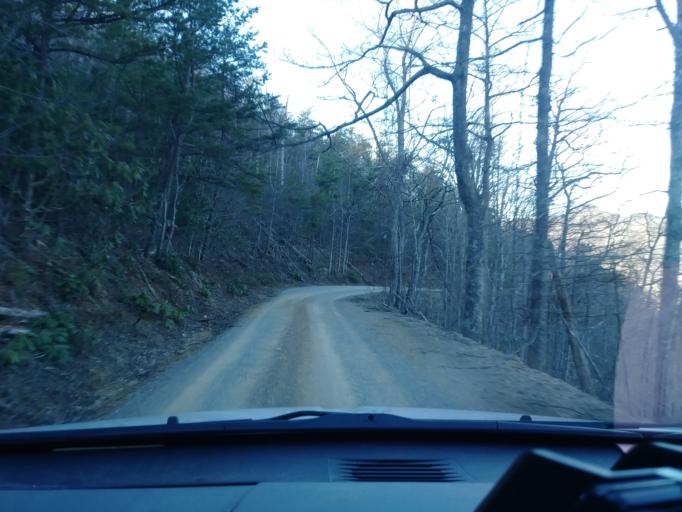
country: US
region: Tennessee
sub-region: Greene County
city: Tusculum
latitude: 36.0772
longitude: -82.6851
